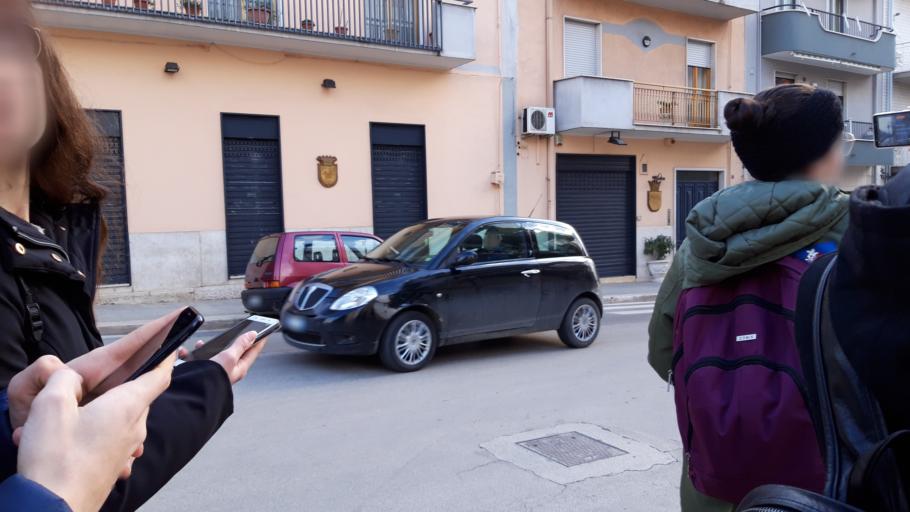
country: IT
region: Apulia
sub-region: Provincia di Barletta - Andria - Trani
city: Andria
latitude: 41.2321
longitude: 16.2893
